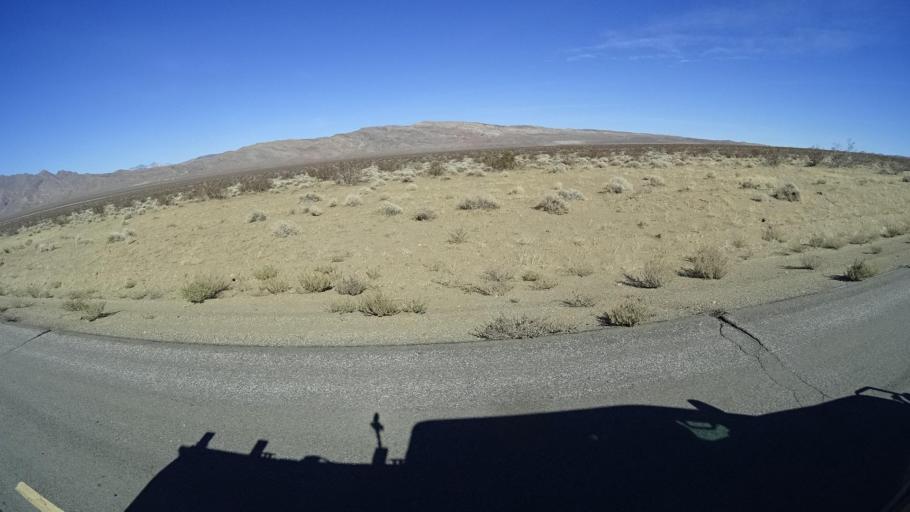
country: US
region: California
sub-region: Kern County
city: Ridgecrest
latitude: 35.3844
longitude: -117.7174
